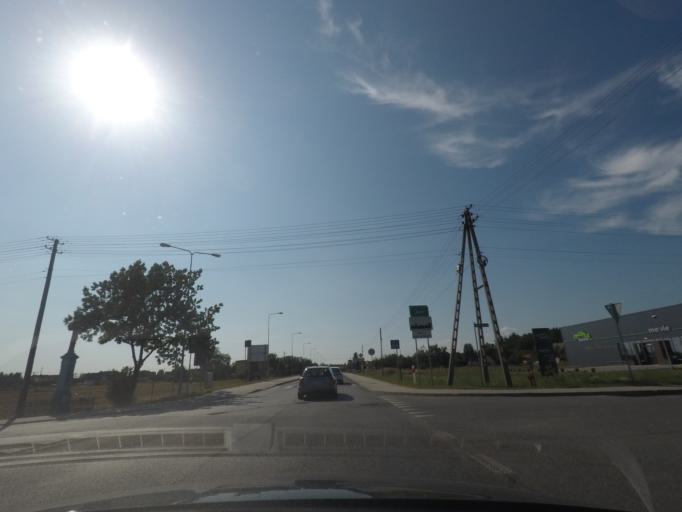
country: PL
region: Silesian Voivodeship
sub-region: Powiat pszczynski
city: Rudziczka
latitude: 50.0372
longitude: 18.7513
